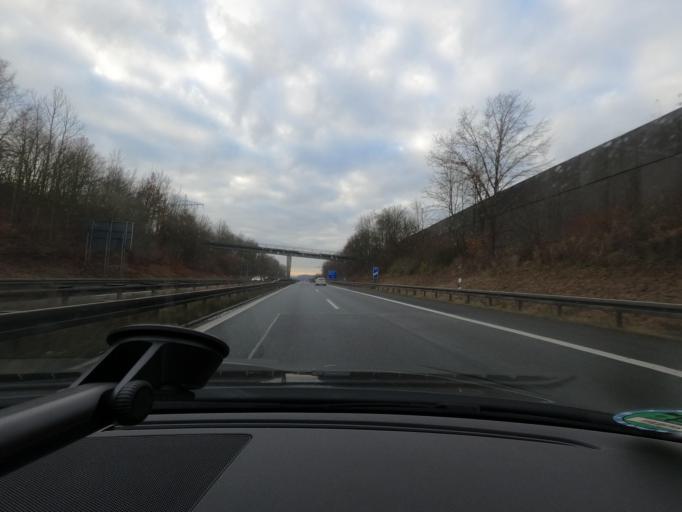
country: DE
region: Bavaria
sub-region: Upper Franconia
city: Bad Staffelstein
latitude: 50.0988
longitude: 11.0079
